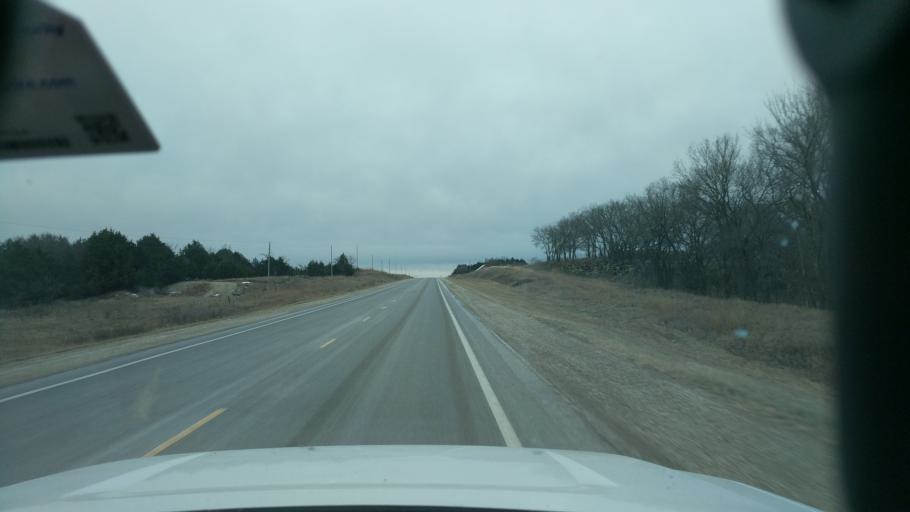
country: US
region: Kansas
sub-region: Marion County
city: Marion
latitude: 38.4639
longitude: -96.9576
